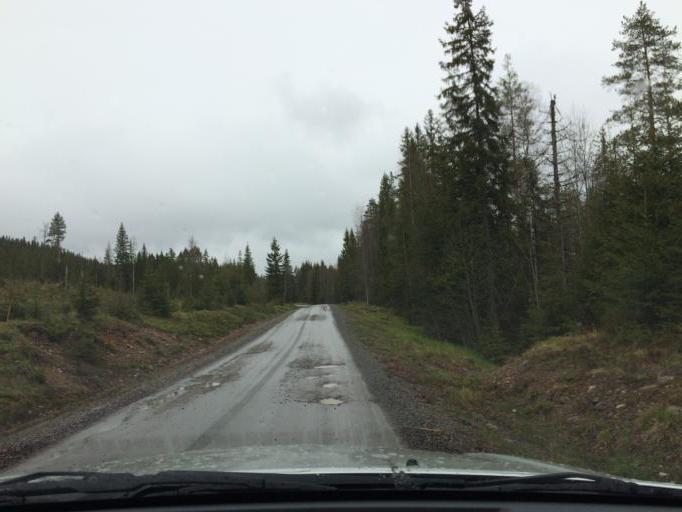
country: SE
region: Dalarna
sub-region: Ludvika Kommun
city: Abborrberget
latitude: 60.0347
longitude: 14.6412
